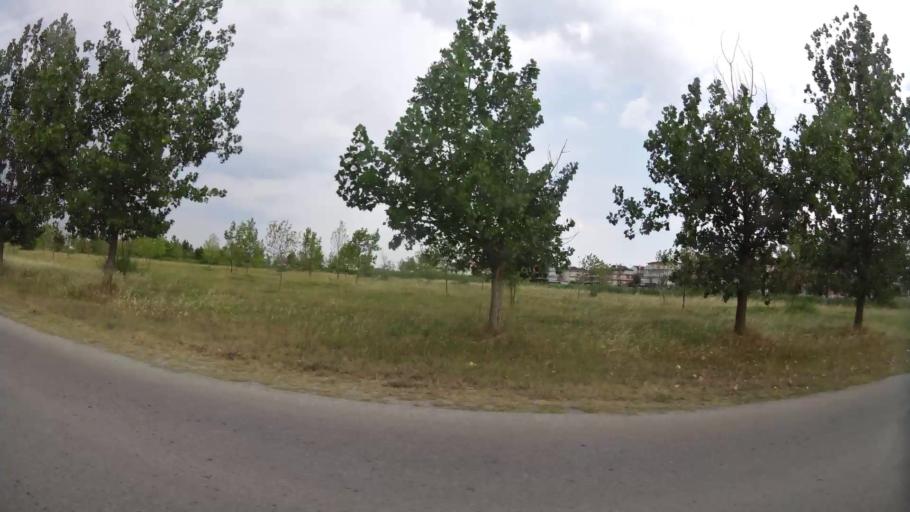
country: GR
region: Central Macedonia
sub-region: Nomos Pierias
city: Paralia
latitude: 40.2742
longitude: 22.5960
